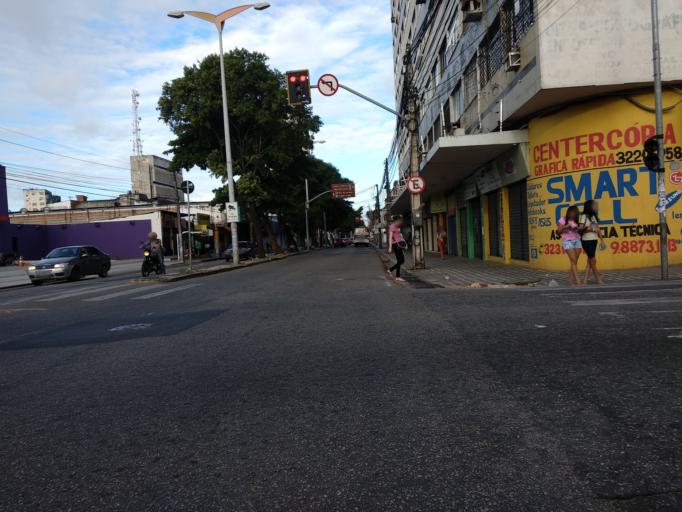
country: BR
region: Ceara
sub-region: Fortaleza
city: Fortaleza
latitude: -3.7310
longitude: -38.5325
